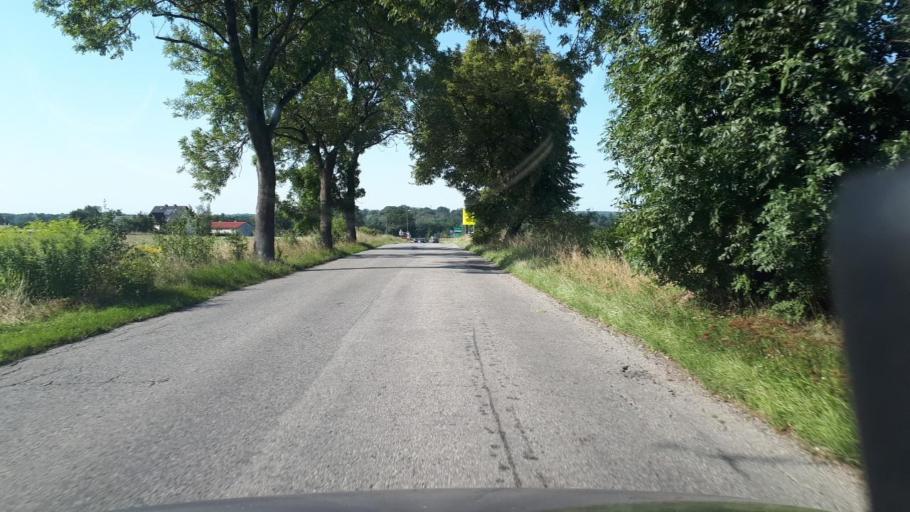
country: PL
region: Silesian Voivodeship
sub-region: Powiat tarnogorski
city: Wieszowa
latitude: 50.3927
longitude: 18.7135
